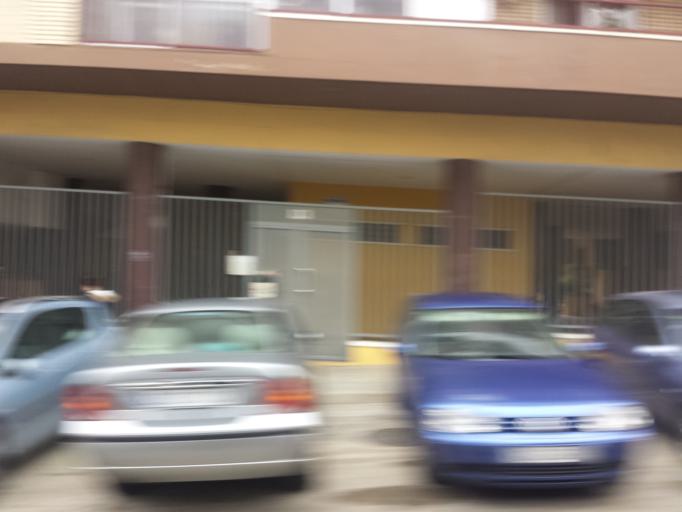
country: ES
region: Aragon
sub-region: Provincia de Zaragoza
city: Zaragoza
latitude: 41.6340
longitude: -0.8784
